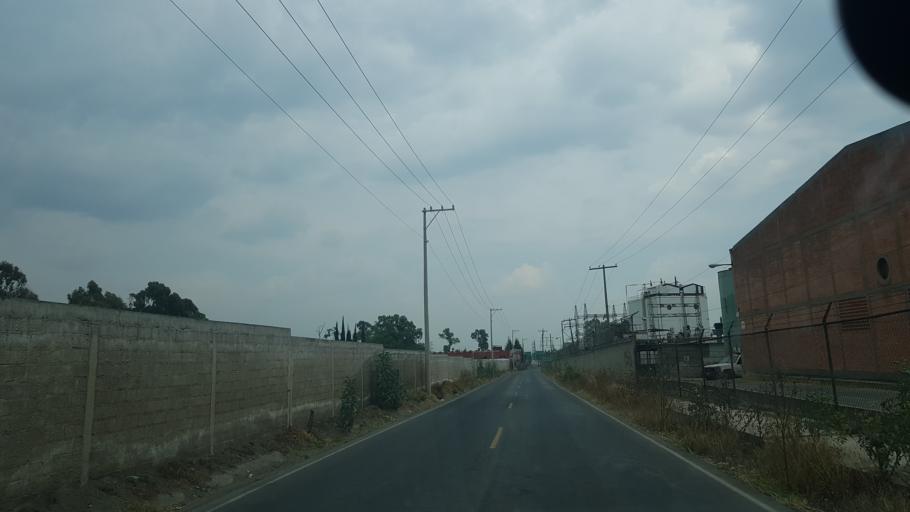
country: MX
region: Puebla
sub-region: Huejotzingo
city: San Mateo Capultitlan
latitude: 19.2024
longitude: -98.4234
